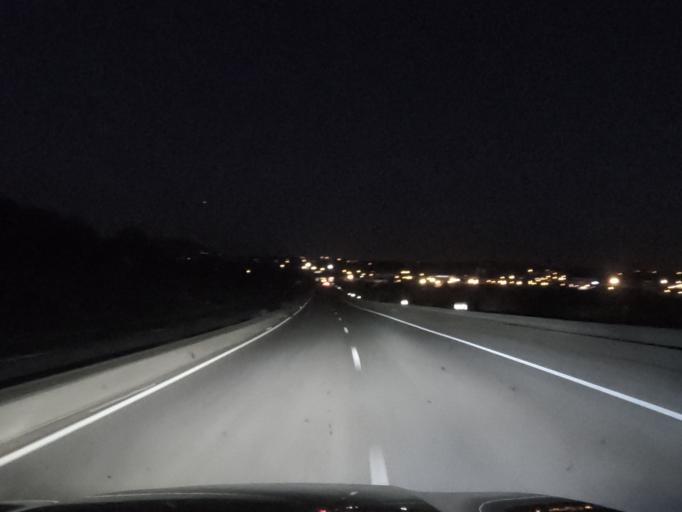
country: PT
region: Faro
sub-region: Loule
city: Loule
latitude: 37.1372
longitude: -8.0436
